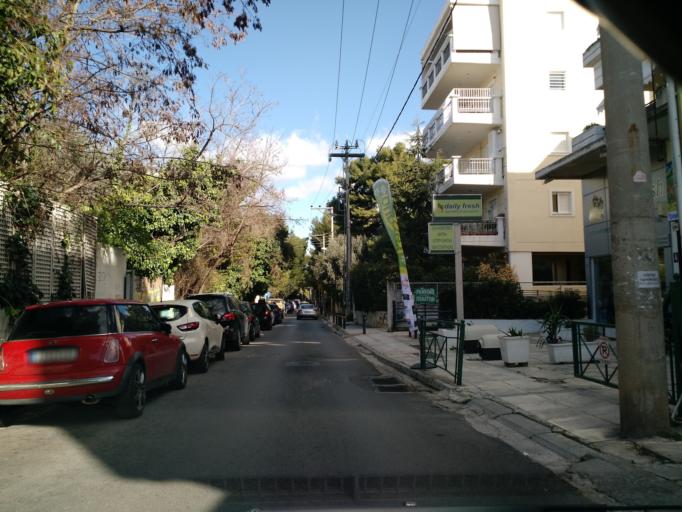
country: GR
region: Attica
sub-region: Nomarchia Athinas
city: Agia Paraskevi
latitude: 38.0067
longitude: 23.8278
